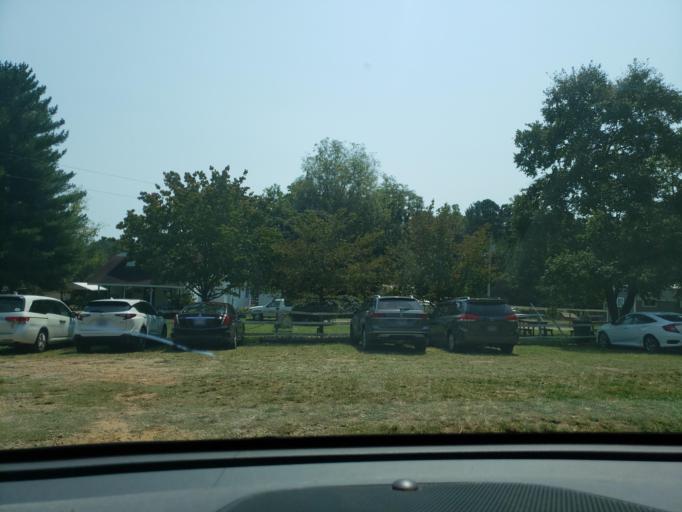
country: US
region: North Carolina
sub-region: Orange County
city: Hillsborough
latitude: 36.0041
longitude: -79.0845
